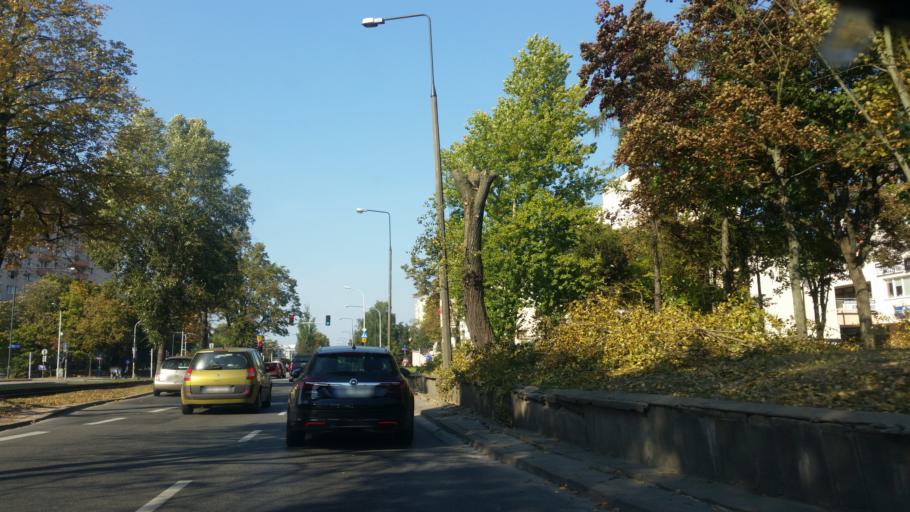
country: PL
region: Masovian Voivodeship
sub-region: Warszawa
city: Bemowo
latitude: 52.2243
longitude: 20.9169
